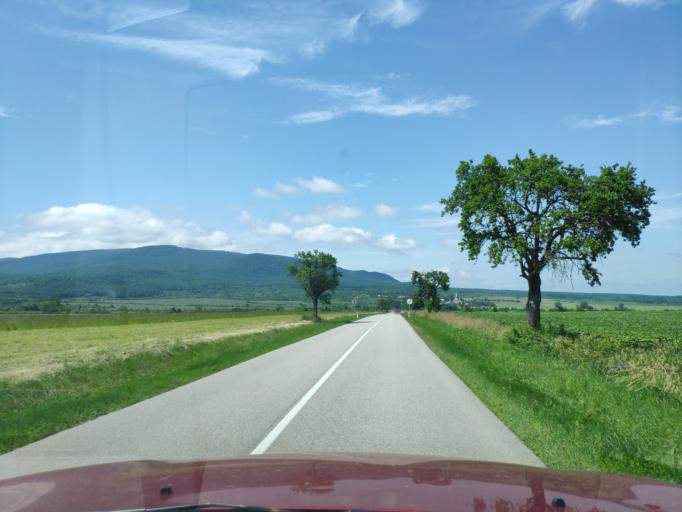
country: SK
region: Kosicky
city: Secovce
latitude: 48.7435
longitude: 21.6459
